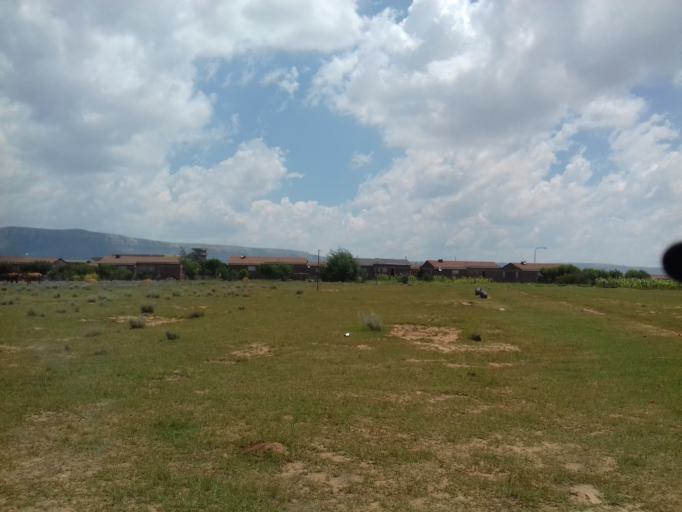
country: LS
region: Maseru
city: Maseru
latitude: -29.4502
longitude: 27.5642
